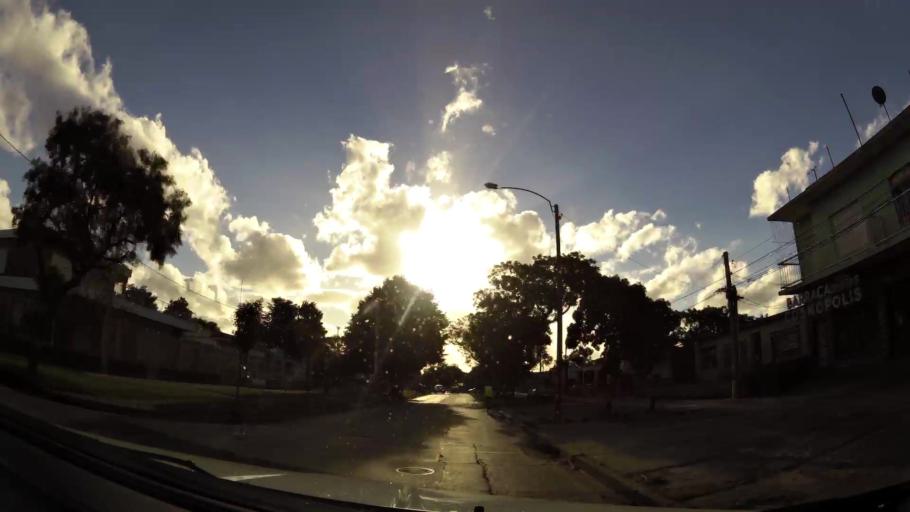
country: UY
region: Montevideo
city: Montevideo
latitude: -34.8756
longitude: -56.2623
